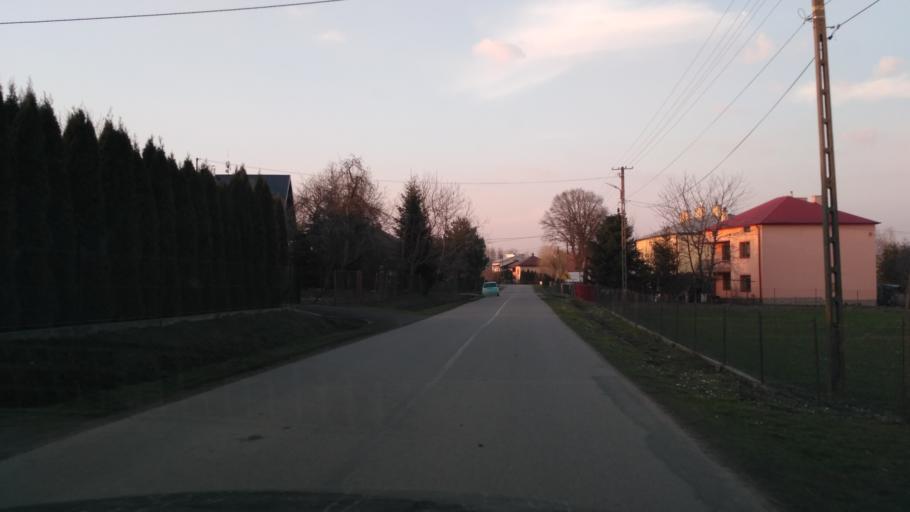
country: PL
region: Subcarpathian Voivodeship
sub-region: Powiat przeworski
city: Zarzecze
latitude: 49.9494
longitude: 22.5565
